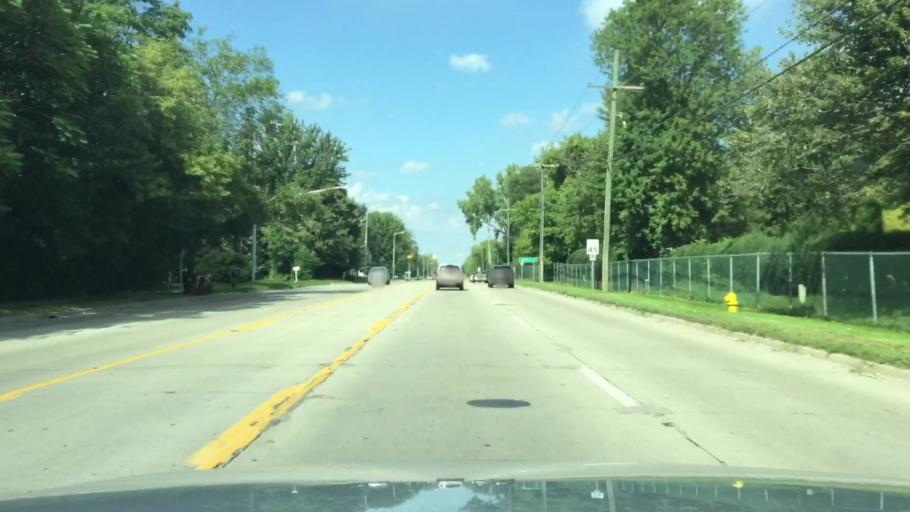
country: US
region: Michigan
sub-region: Wayne County
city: Wayne
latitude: 42.2729
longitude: -83.3481
